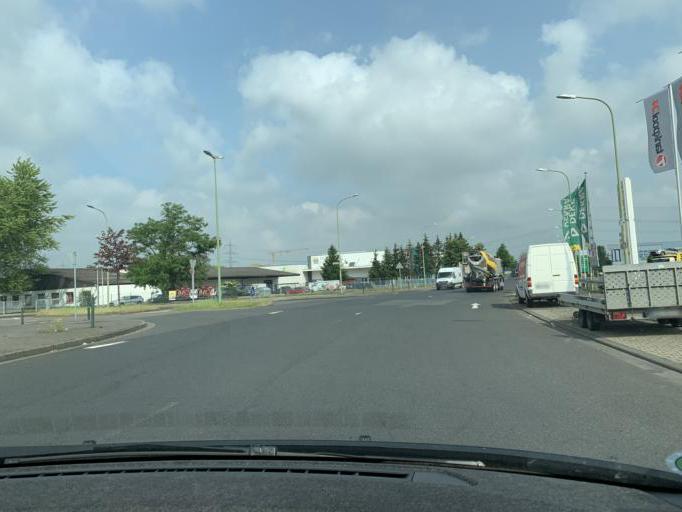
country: DE
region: North Rhine-Westphalia
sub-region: Regierungsbezirk Koln
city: Dueren
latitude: 50.8342
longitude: 6.4622
